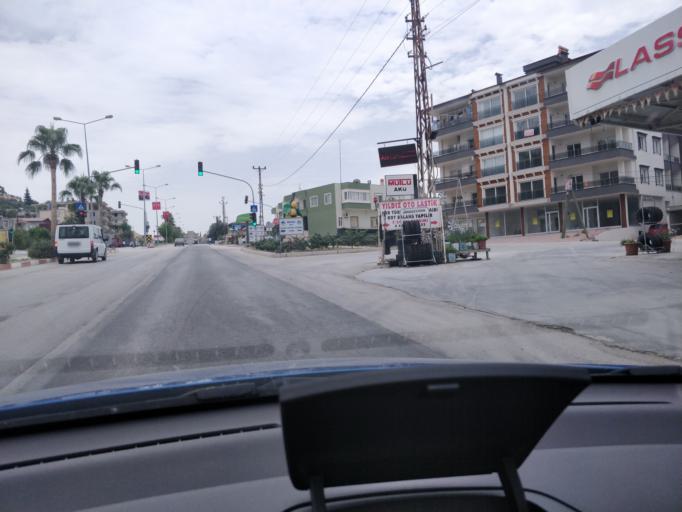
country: TR
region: Mersin
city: Mut
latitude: 36.6506
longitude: 33.4256
